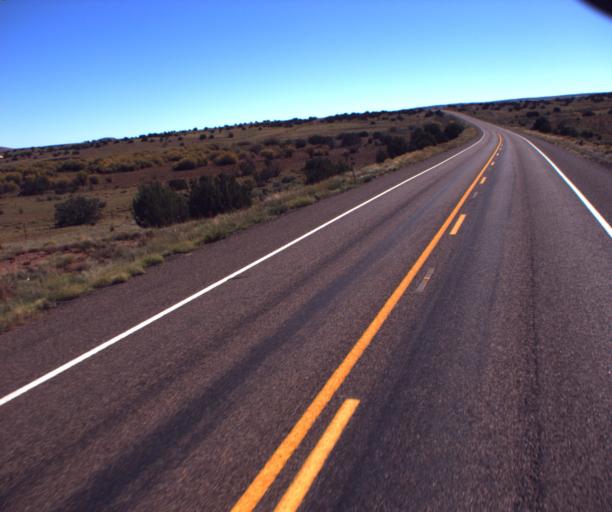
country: US
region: Arizona
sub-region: Apache County
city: Saint Johns
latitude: 34.5984
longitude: -109.6342
